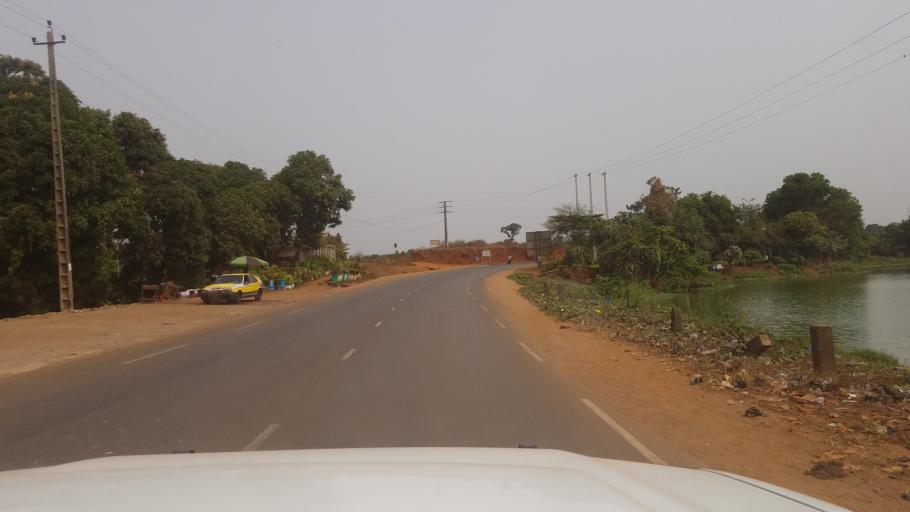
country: GN
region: Kindia
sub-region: Prefecture de Dubreka
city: Dubreka
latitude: 9.6743
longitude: -13.5838
